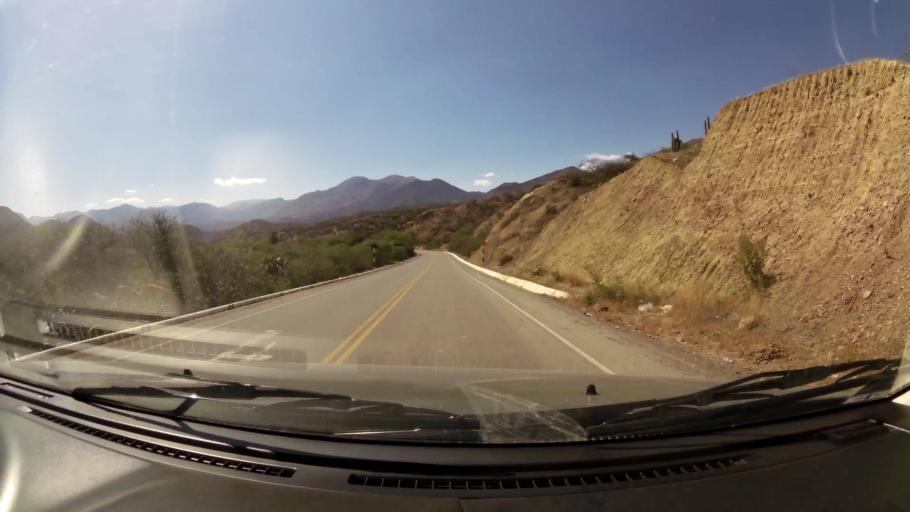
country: PE
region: Ayacucho
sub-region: Provincia de Huanta
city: Luricocha
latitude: -12.8931
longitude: -74.3137
